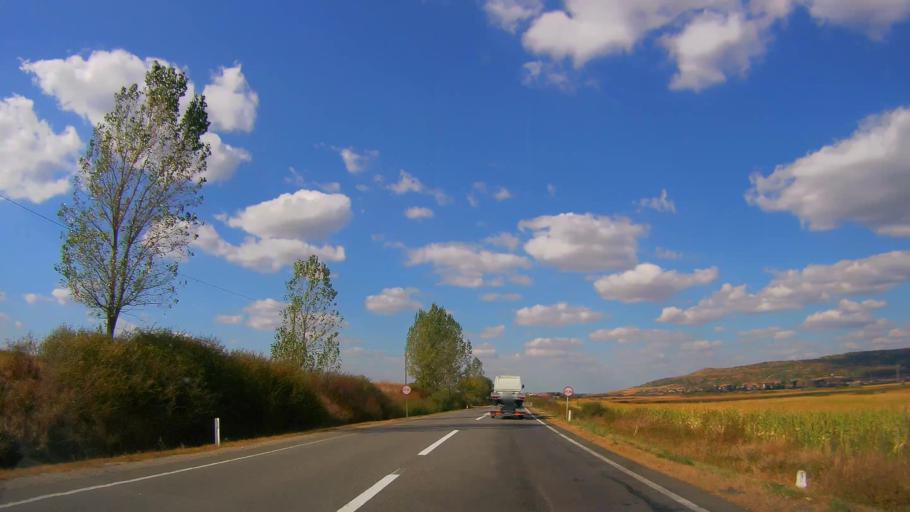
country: RO
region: Salaj
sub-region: Comuna Bobota
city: Dersida
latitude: 47.3698
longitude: 22.7893
